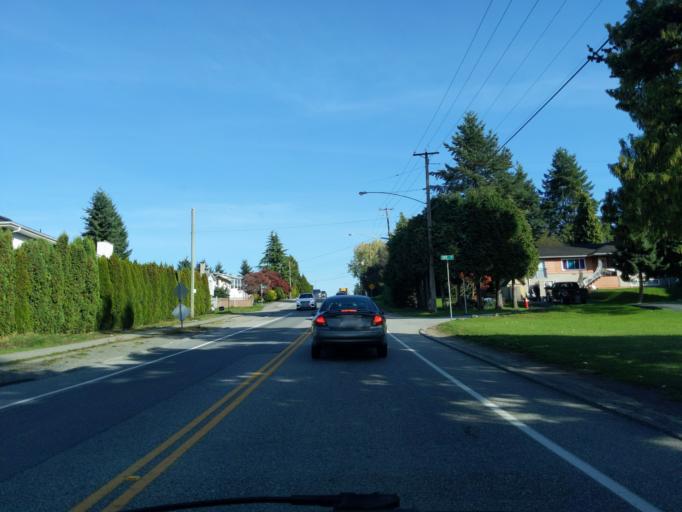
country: CA
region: British Columbia
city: New Westminster
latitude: 49.1917
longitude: -122.8718
